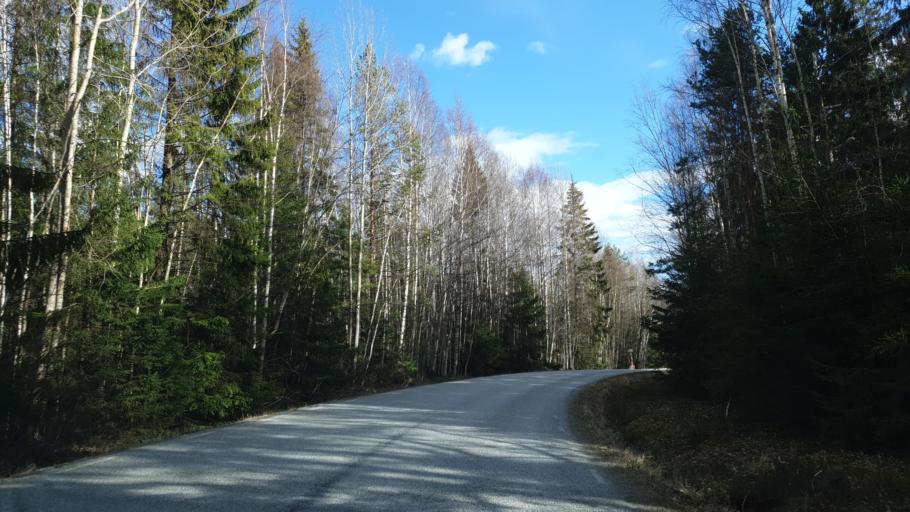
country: SE
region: Stockholm
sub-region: Varmdo Kommun
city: Mortnas
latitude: 59.2419
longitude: 18.4715
